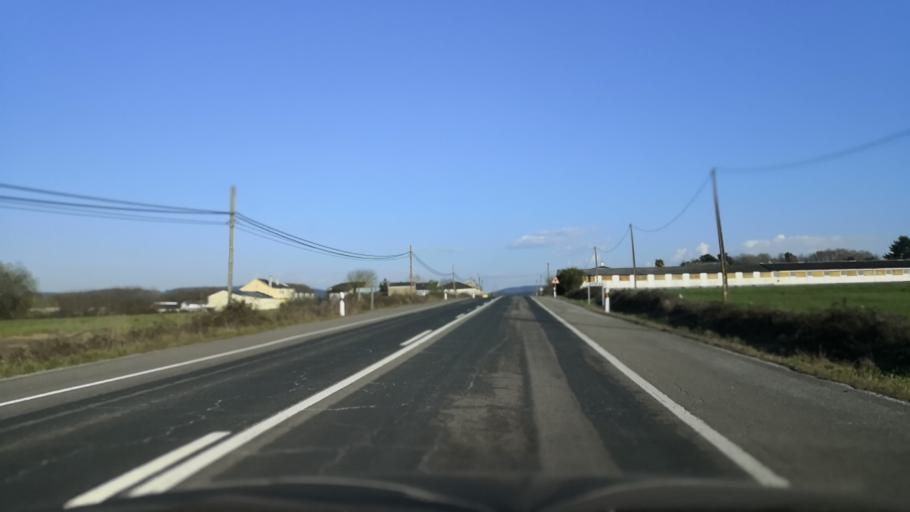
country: ES
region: Galicia
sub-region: Provincia de Lugo
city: Corgo
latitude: 42.9350
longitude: -7.4052
